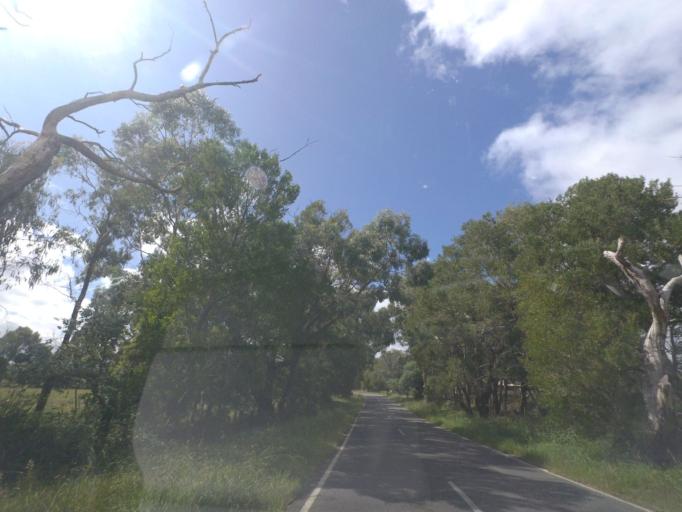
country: AU
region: Victoria
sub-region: Yarra Ranges
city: Launching Place
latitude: -37.7890
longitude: 145.5685
